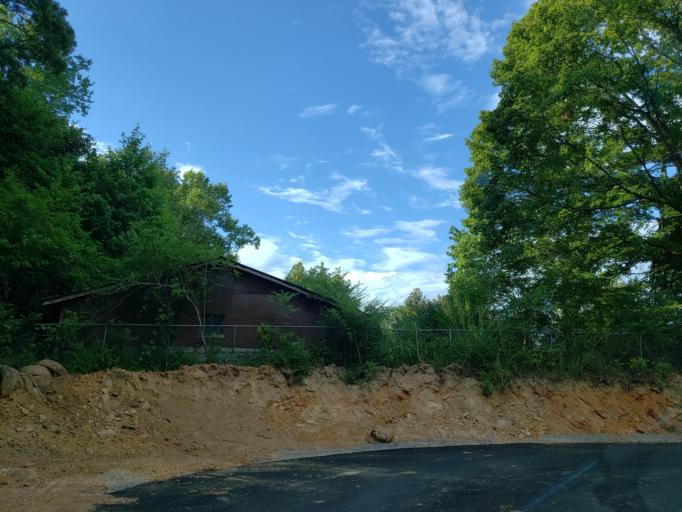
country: US
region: Georgia
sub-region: Cherokee County
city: Ball Ground
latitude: 34.3439
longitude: -84.3786
